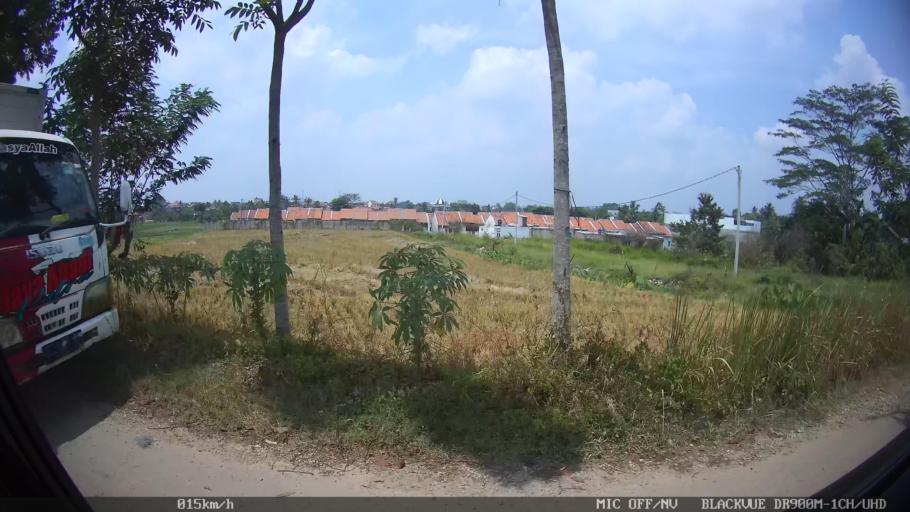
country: ID
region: Lampung
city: Pringsewu
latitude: -5.3397
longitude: 104.9771
